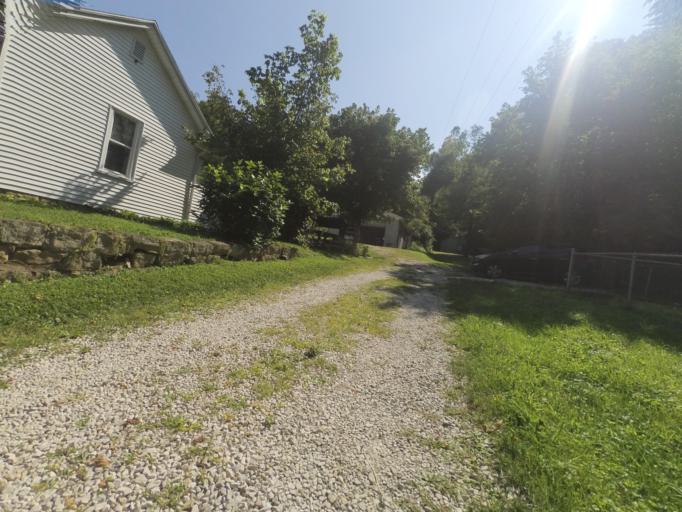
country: US
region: West Virginia
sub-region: Cabell County
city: Huntington
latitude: 38.3919
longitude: -82.4676
